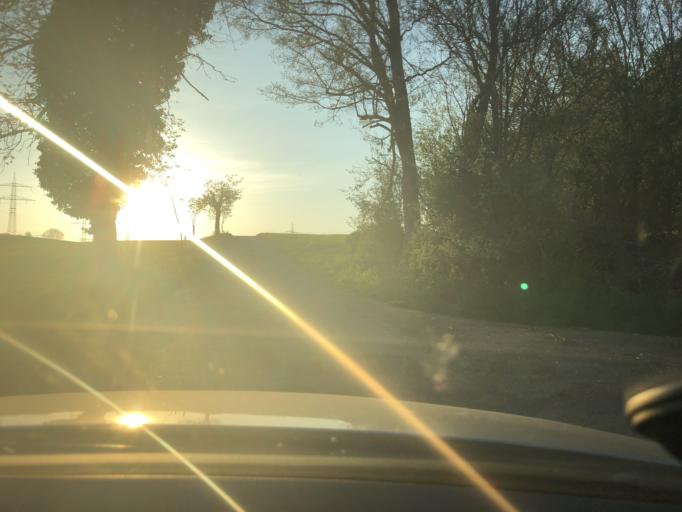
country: DE
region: Baden-Wuerttemberg
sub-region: Freiburg Region
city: Waldshut-Tiengen
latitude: 47.6498
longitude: 8.1875
